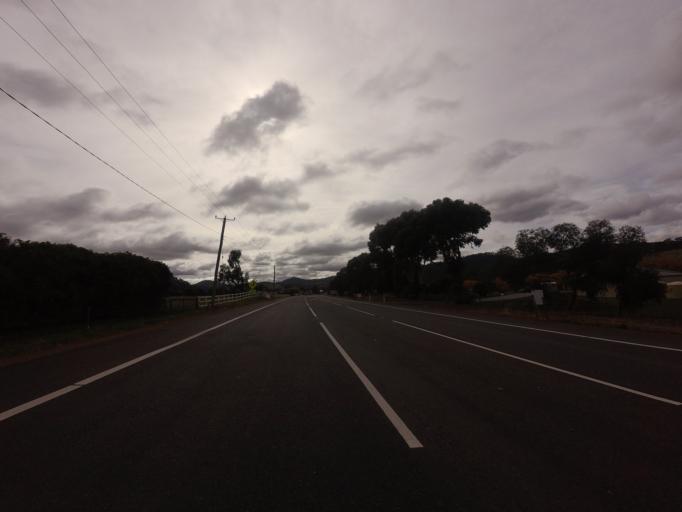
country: AU
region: Tasmania
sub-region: Brighton
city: Bridgewater
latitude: -42.6196
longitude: 147.2220
